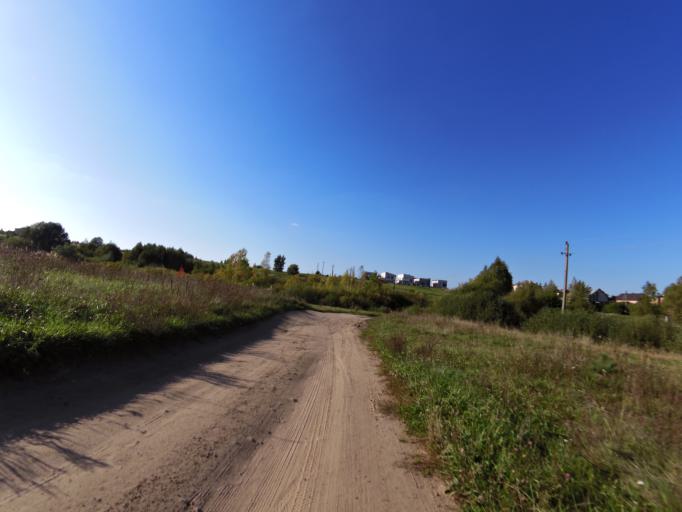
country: LT
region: Vilnius County
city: Pilaite
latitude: 54.7211
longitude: 25.1810
